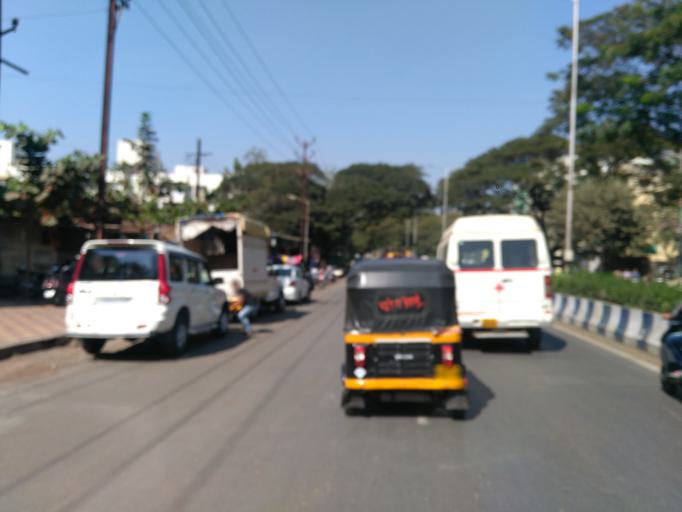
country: IN
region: Maharashtra
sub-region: Pune Division
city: Pune
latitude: 18.4698
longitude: 73.8639
